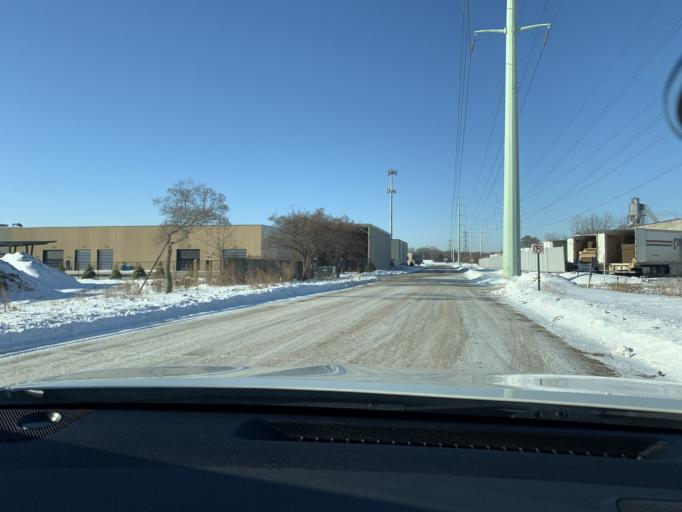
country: US
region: Minnesota
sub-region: Anoka County
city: Fridley
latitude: 45.0968
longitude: -93.2585
